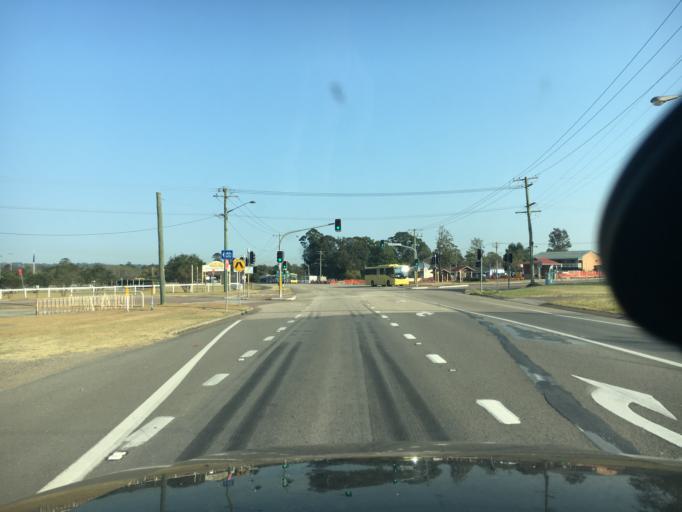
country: AU
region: New South Wales
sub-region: Cessnock
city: Branxton
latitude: -32.6577
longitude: 151.3619
